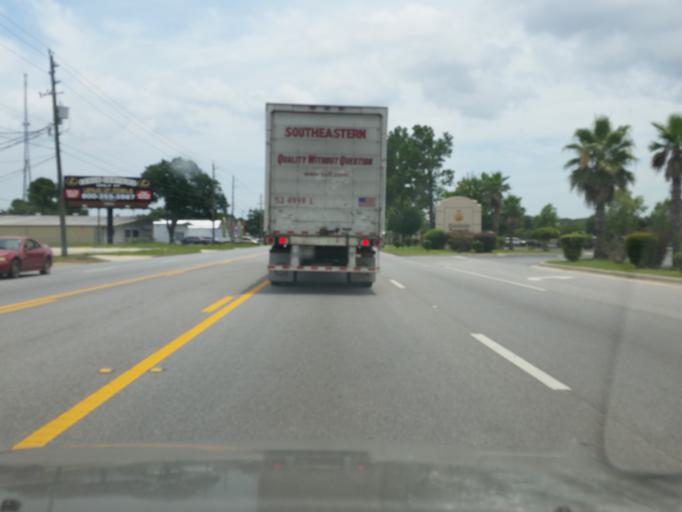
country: US
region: Florida
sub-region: Escambia County
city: Brent
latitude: 30.4788
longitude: -87.2574
